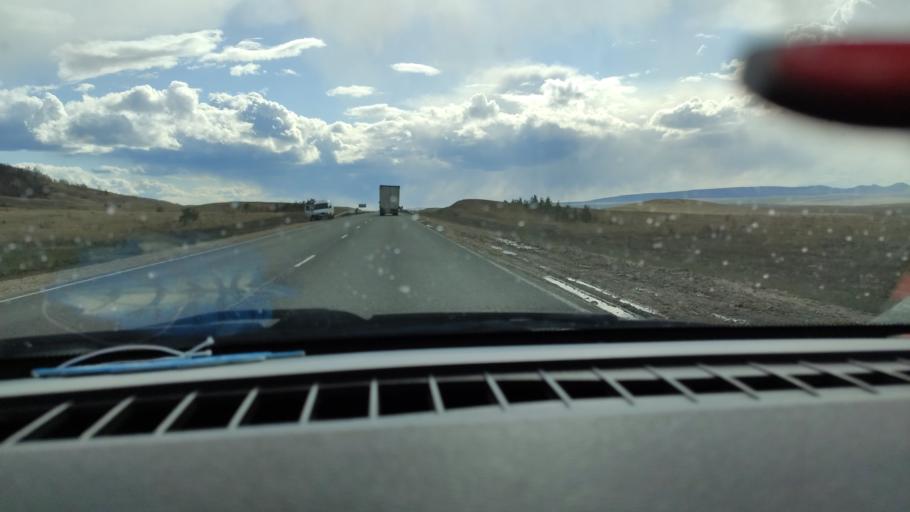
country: RU
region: Saratov
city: Alekseyevka
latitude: 52.3596
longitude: 47.9518
